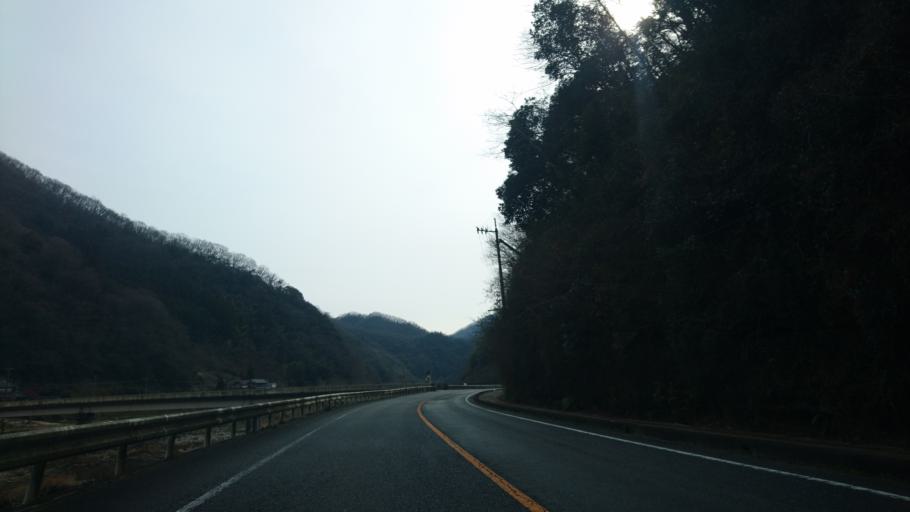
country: JP
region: Okayama
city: Takahashi
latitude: 34.8734
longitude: 133.5622
